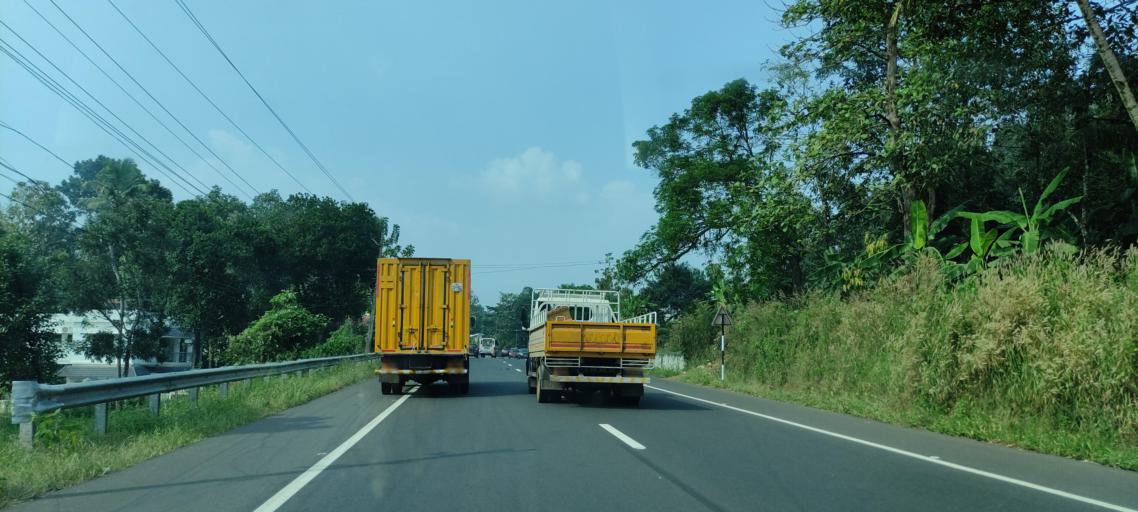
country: IN
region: Kerala
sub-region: Alappuzha
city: Chengannur
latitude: 9.2638
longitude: 76.6563
